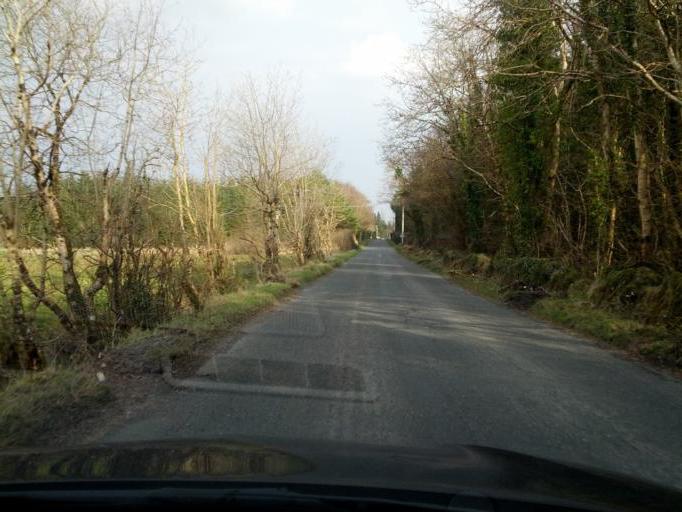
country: IE
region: Connaught
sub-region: County Galway
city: Athenry
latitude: 53.4655
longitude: -8.5382
